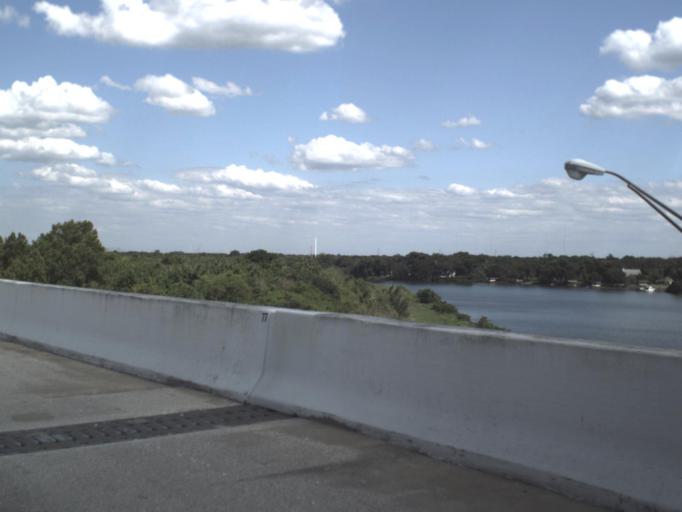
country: US
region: Florida
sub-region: Hillsborough County
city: Palm River-Clair Mel
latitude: 27.9504
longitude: -82.3845
